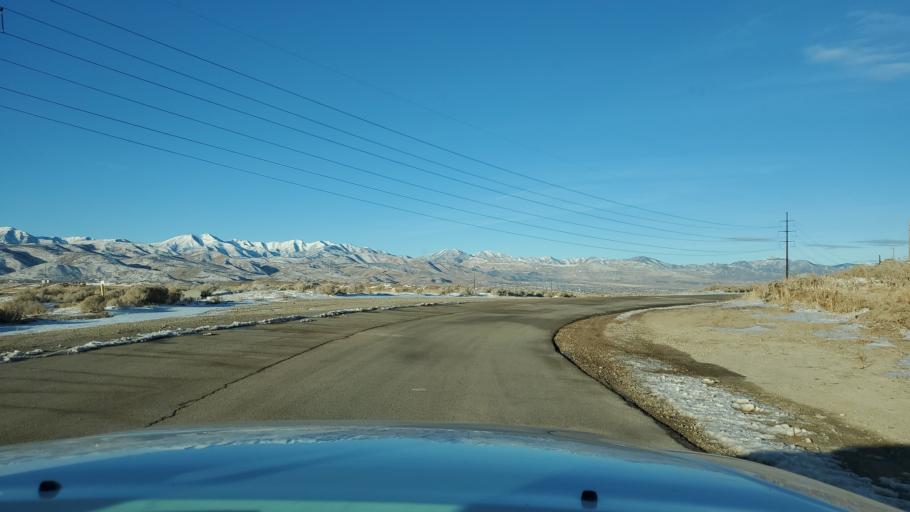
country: US
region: Utah
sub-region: Salt Lake County
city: Bluffdale
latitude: 40.4592
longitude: -111.8969
